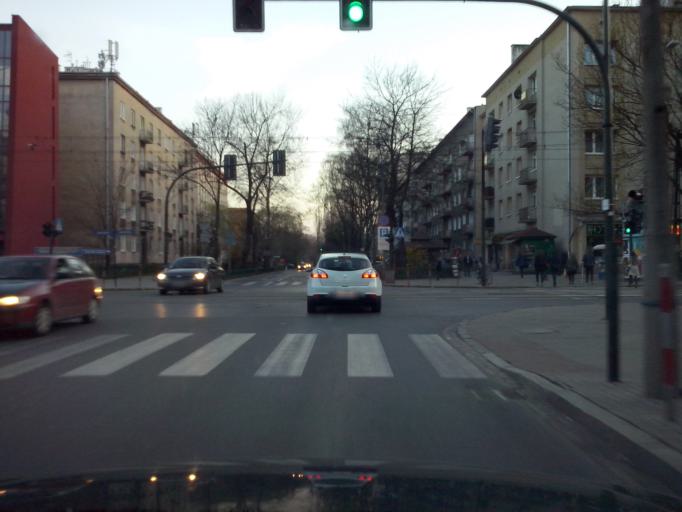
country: PL
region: Lesser Poland Voivodeship
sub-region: Krakow
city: Krakow
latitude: 50.0734
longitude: 19.9156
